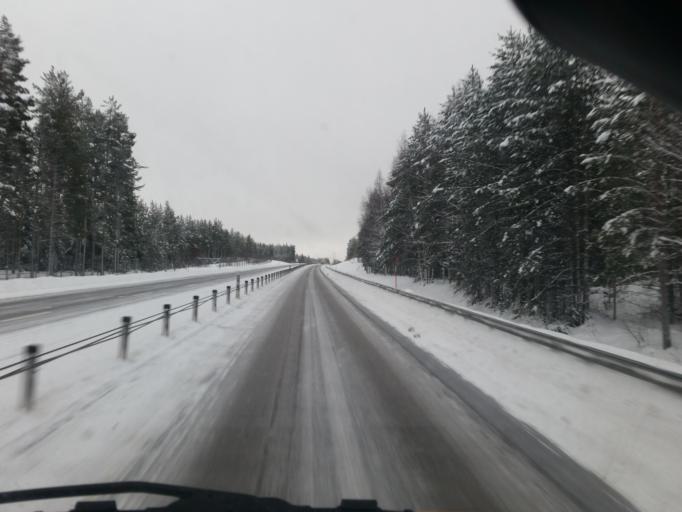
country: SE
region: Norrbotten
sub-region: Pitea Kommun
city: Pitea
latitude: 65.2823
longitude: 21.4435
